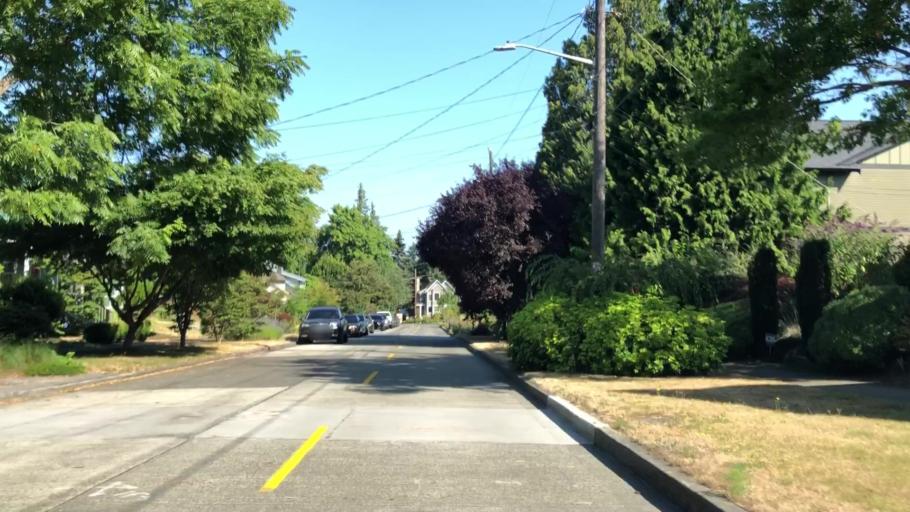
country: US
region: Washington
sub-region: King County
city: Seattle
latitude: 47.6704
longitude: -122.3327
